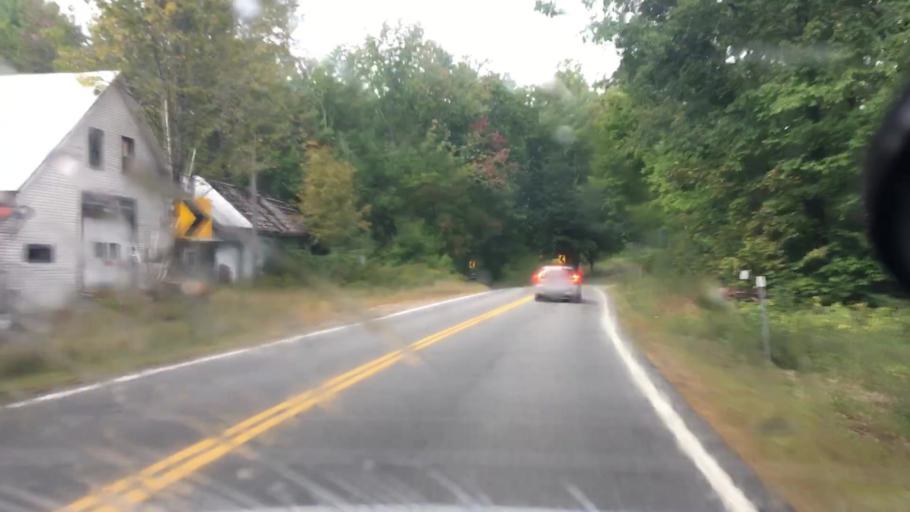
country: US
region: Maine
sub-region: York County
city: Parsonsfield
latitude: 43.6644
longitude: -70.9903
